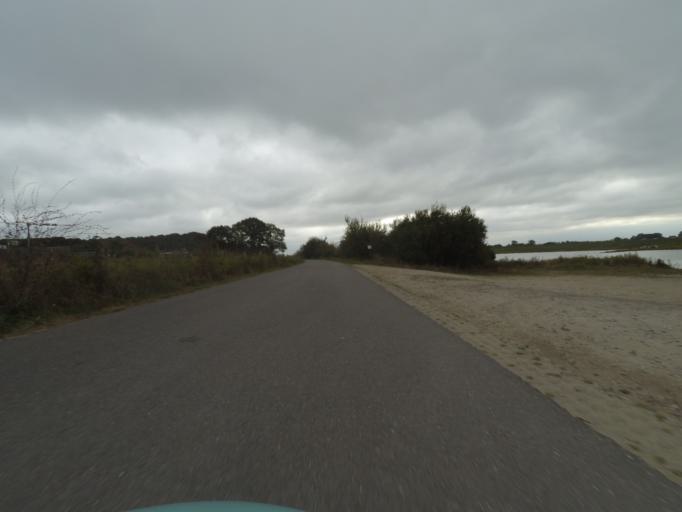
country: NL
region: Utrecht
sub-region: Gemeente Rhenen
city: Rhenen
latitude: 51.9532
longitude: 5.5804
